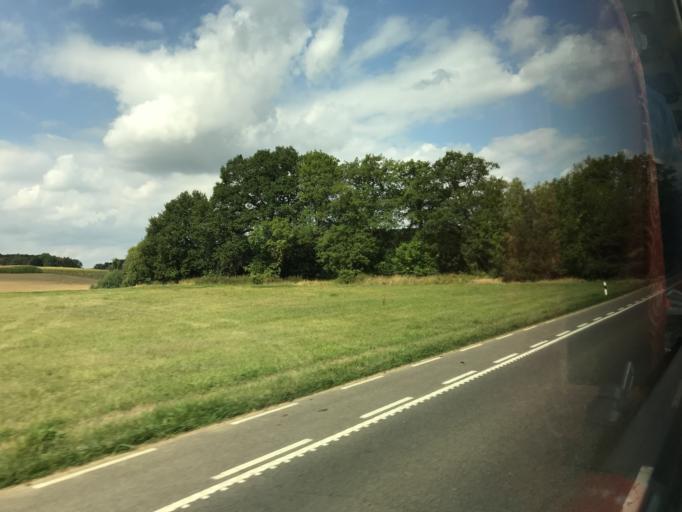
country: LU
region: Luxembourg
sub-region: Canton de Luxembourg
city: Weiler-la-Tour
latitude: 49.5378
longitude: 6.1774
